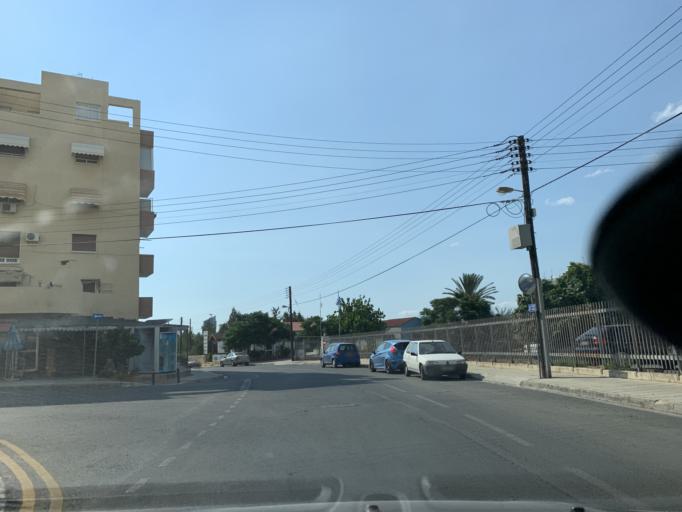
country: CY
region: Lefkosia
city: Nicosia
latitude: 35.1541
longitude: 33.3621
